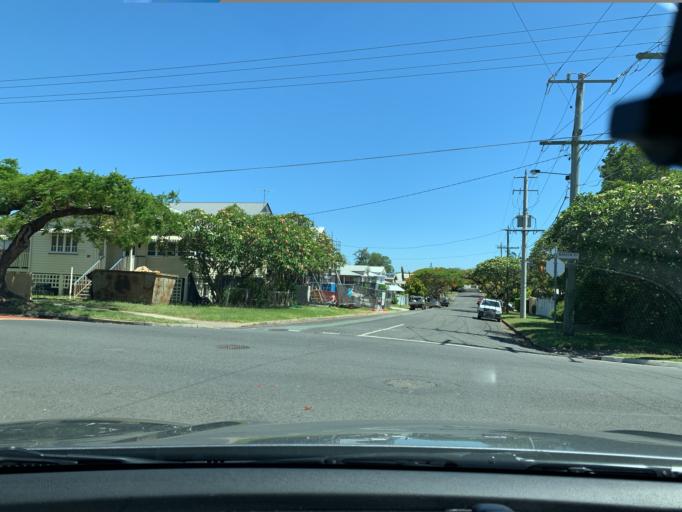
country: AU
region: Queensland
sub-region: Brisbane
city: Ascot
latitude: -27.4221
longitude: 153.0654
